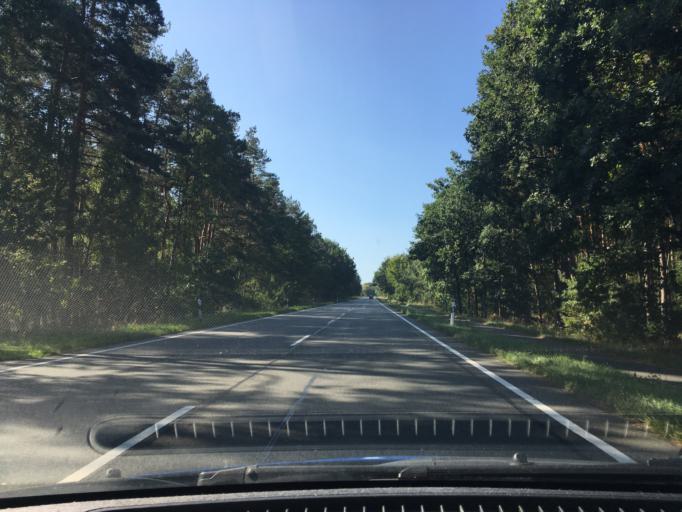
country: DE
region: Lower Saxony
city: Betzendorf
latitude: 53.1604
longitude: 10.3013
